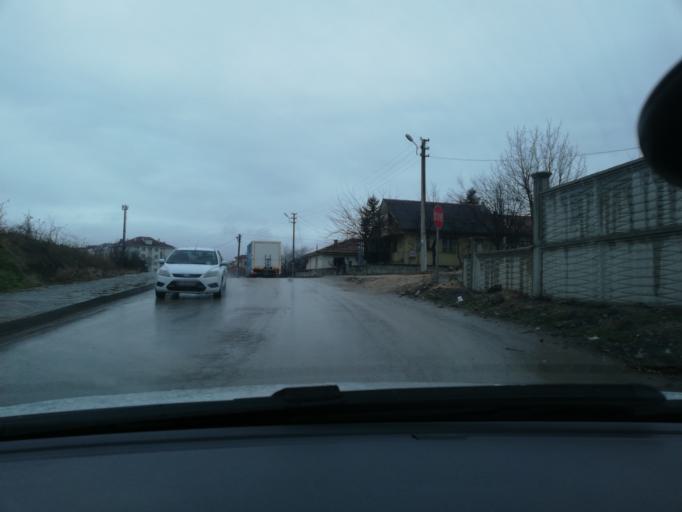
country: TR
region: Bolu
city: Bolu
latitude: 40.7354
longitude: 31.6334
